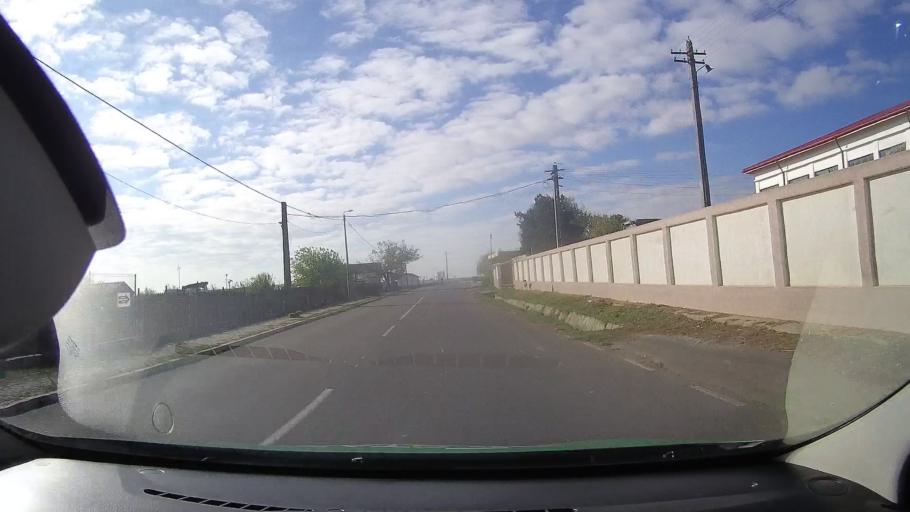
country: RO
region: Tulcea
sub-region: Comuna Mahmudia
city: Mahmudia
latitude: 45.0801
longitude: 29.0799
